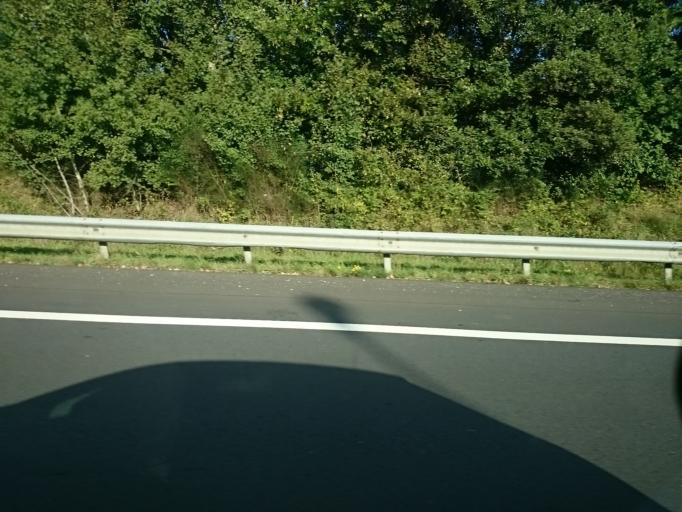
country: FR
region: Pays de la Loire
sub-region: Departement de la Loire-Atlantique
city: Saint-Herblain
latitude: 47.2074
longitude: -1.6258
